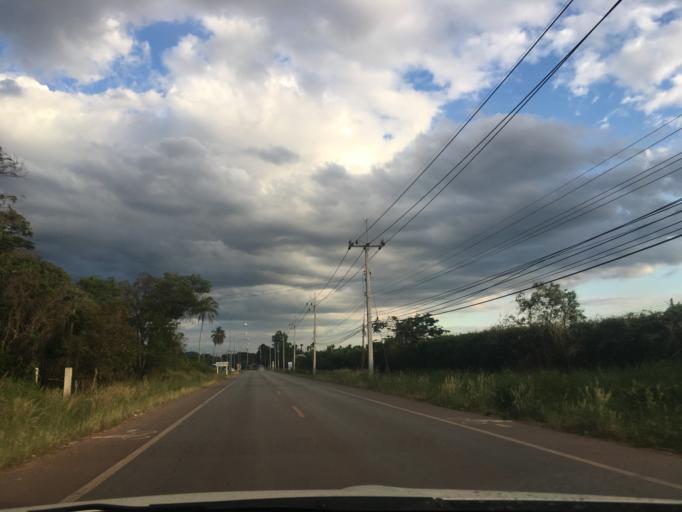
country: TH
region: Chanthaburi
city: Na Yai Am
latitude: 12.6839
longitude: 101.8257
